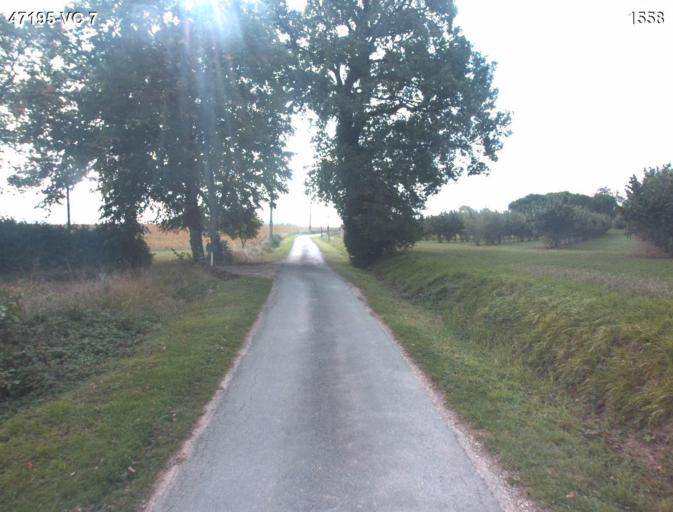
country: FR
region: Aquitaine
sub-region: Departement du Lot-et-Garonne
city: Nerac
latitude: 44.1028
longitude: 0.3400
